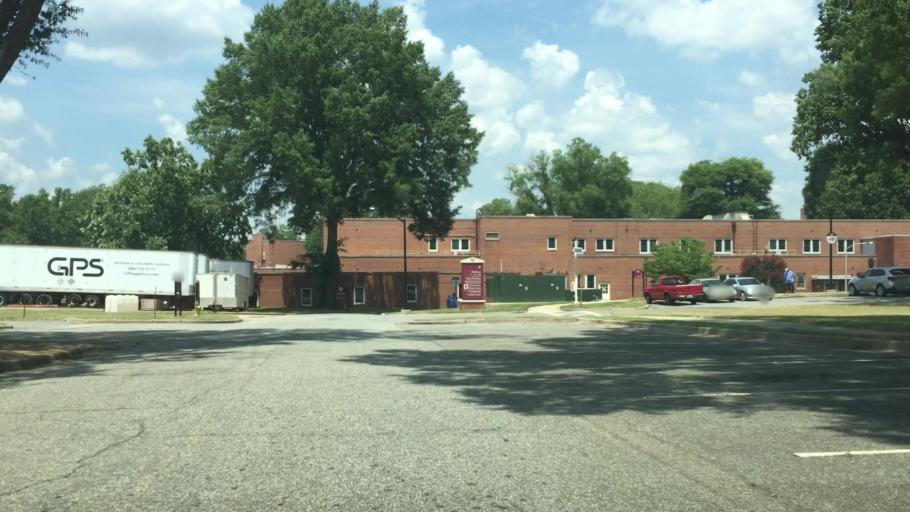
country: US
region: North Carolina
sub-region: Rowan County
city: Salisbury
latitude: 35.6836
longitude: -80.4898
